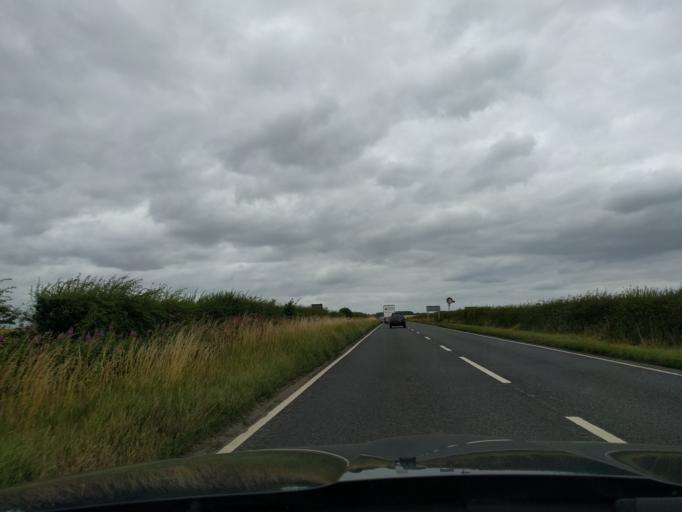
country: GB
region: England
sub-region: Northumberland
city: Ancroft
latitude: 55.7065
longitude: -1.9699
